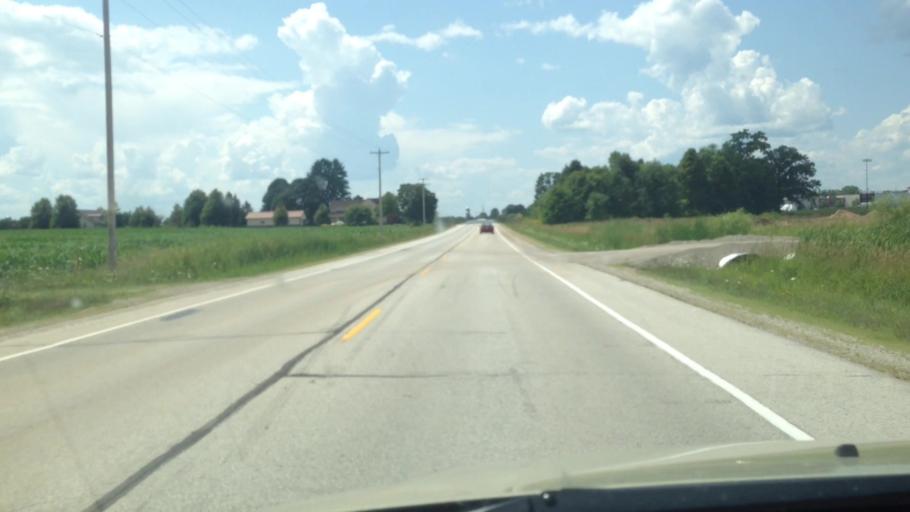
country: US
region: Wisconsin
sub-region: Brown County
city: Pulaski
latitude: 44.6569
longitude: -88.2301
